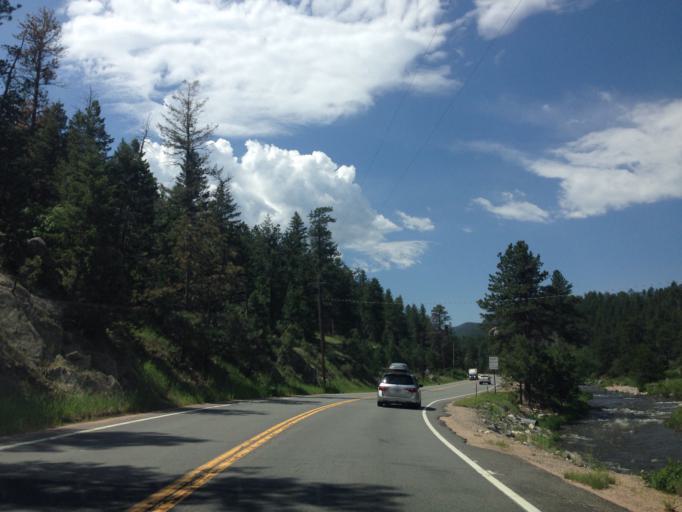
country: US
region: Colorado
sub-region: Larimer County
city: Estes Park
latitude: 40.4043
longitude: -105.4155
